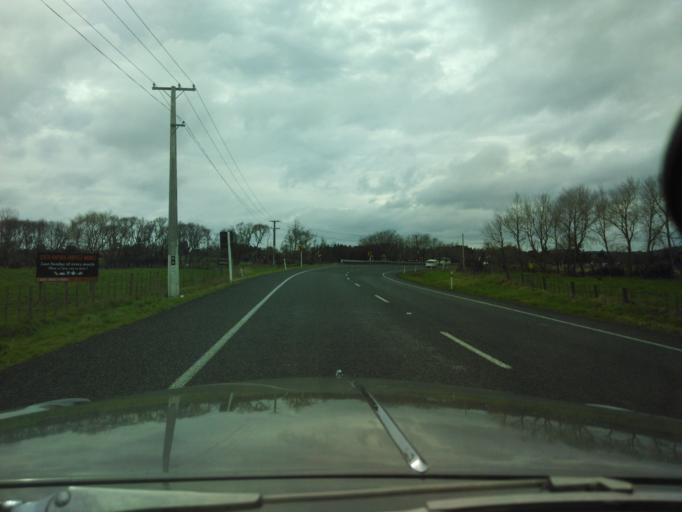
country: NZ
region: Auckland
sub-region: Auckland
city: Parakai
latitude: -36.6903
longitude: 174.4289
